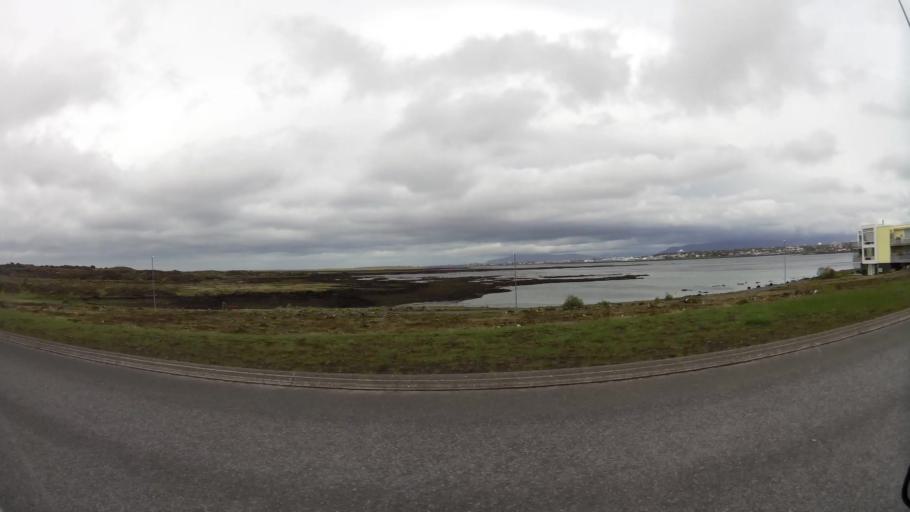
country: IS
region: Capital Region
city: Hafnarfjoerdur
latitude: 64.0922
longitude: -21.9522
